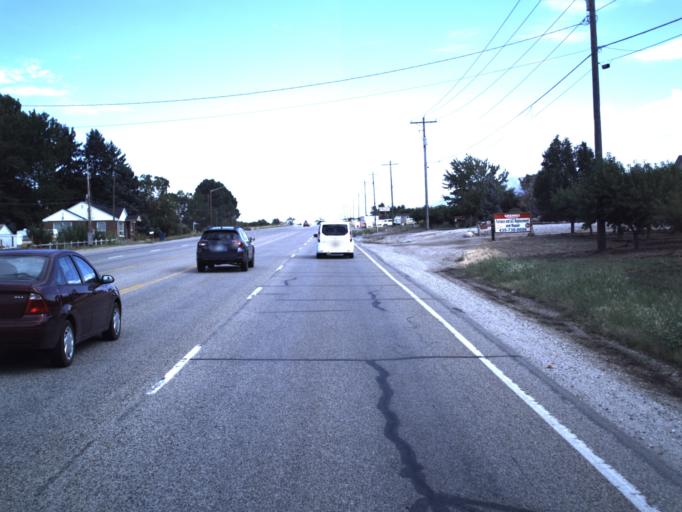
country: US
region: Utah
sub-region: Box Elder County
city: Perry
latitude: 41.4458
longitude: -112.0374
